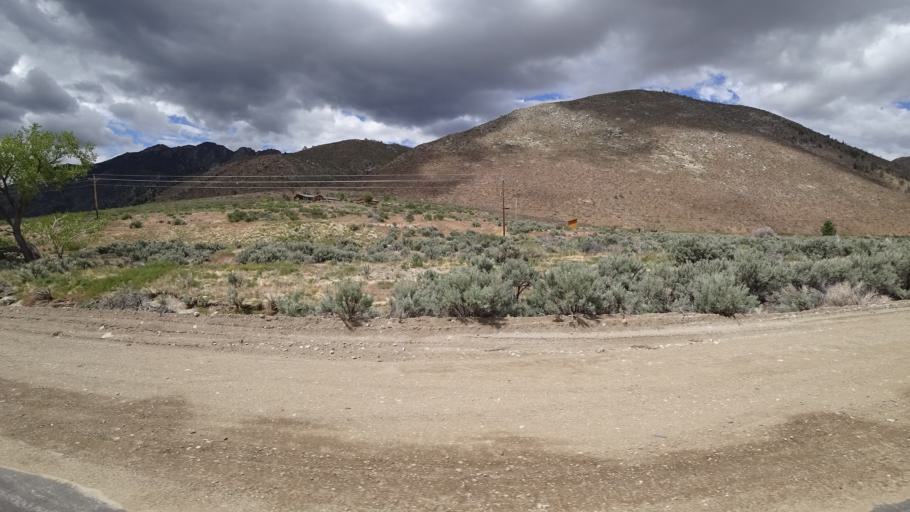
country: US
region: Nevada
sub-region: Lyon County
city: Smith Valley
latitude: 38.6350
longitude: -119.5240
